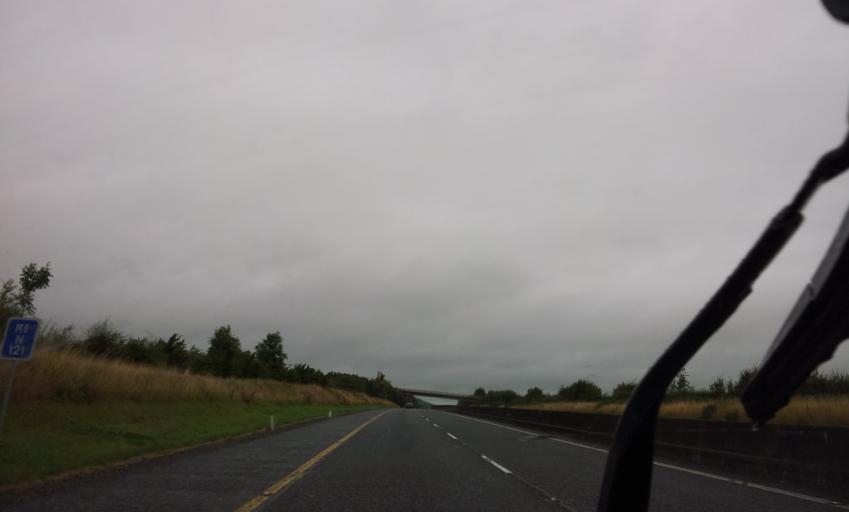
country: IE
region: Munster
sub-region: County Cork
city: Rathcormac
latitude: 52.0845
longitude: -8.2954
